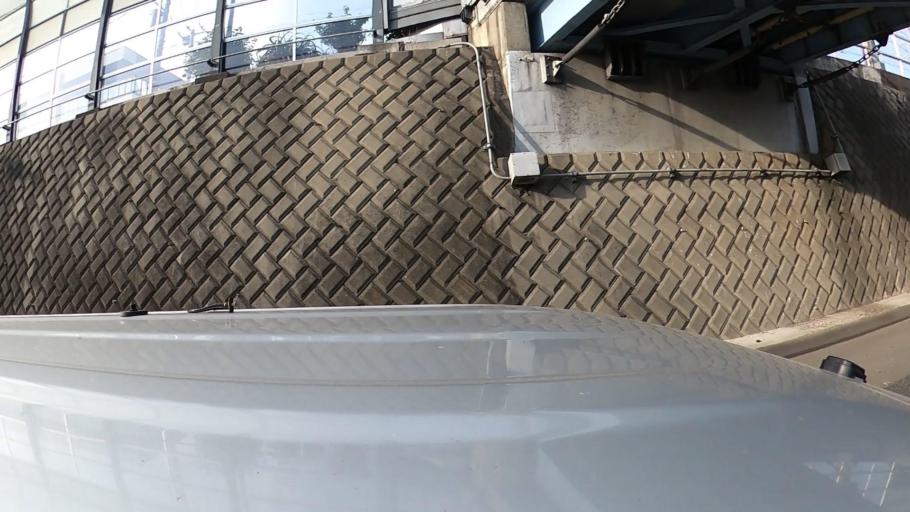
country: JP
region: Saitama
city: Asaka
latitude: 35.7650
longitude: 139.5792
